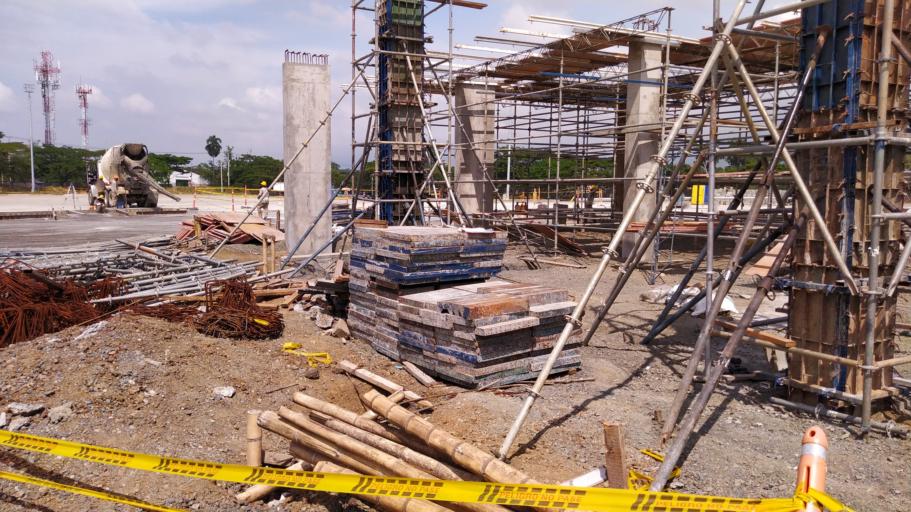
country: CO
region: Valle del Cauca
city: Cali
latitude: 3.3606
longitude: -76.5210
